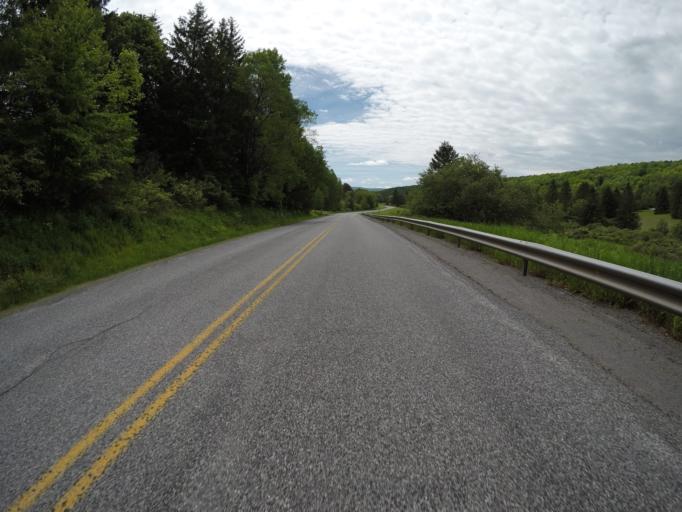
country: US
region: New York
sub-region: Delaware County
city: Stamford
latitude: 42.2290
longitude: -74.5629
